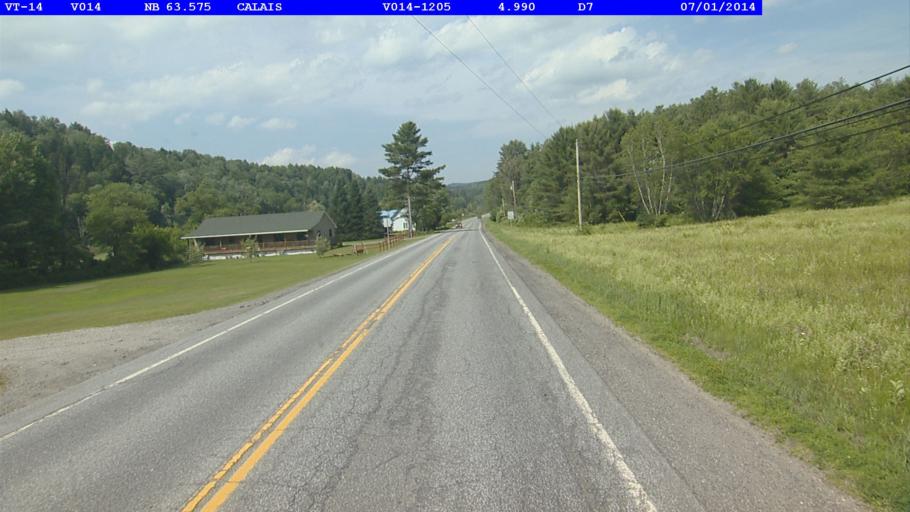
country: US
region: Vermont
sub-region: Caledonia County
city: Hardwick
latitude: 44.3704
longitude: -72.4244
